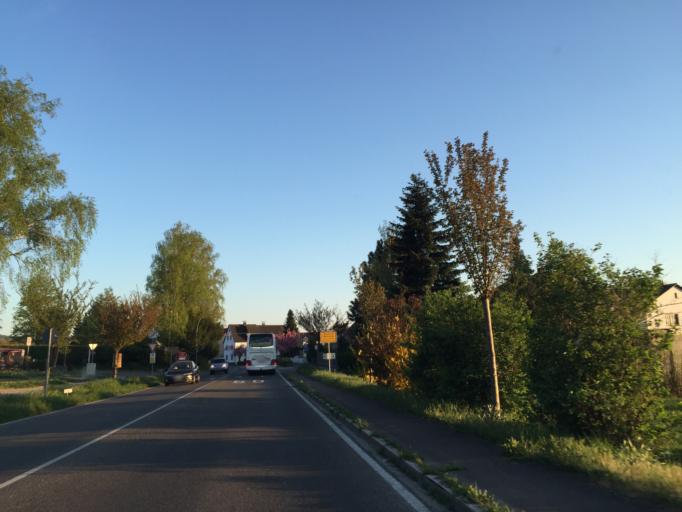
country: DE
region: Baden-Wuerttemberg
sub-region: Karlsruhe Region
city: Hemsbach
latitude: 49.5830
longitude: 8.6575
